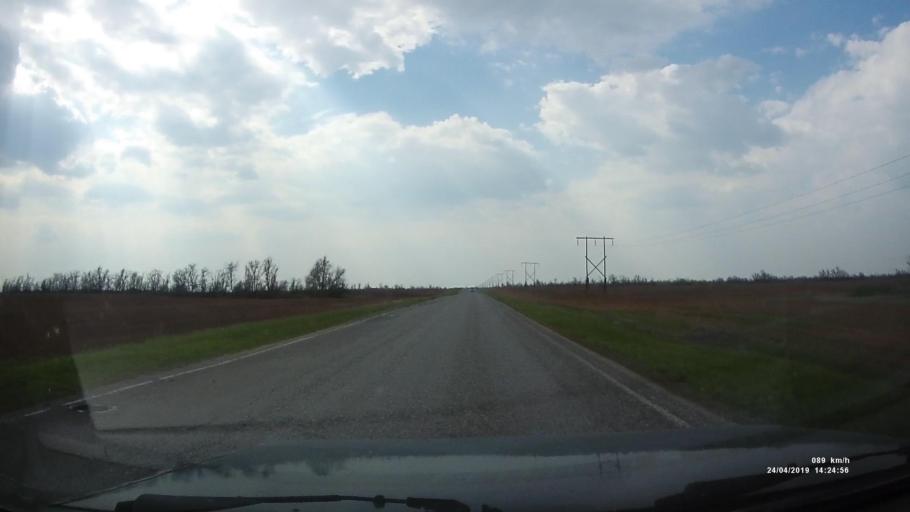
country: RU
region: Kalmykiya
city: Arshan'
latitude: 46.3295
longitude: 44.0884
